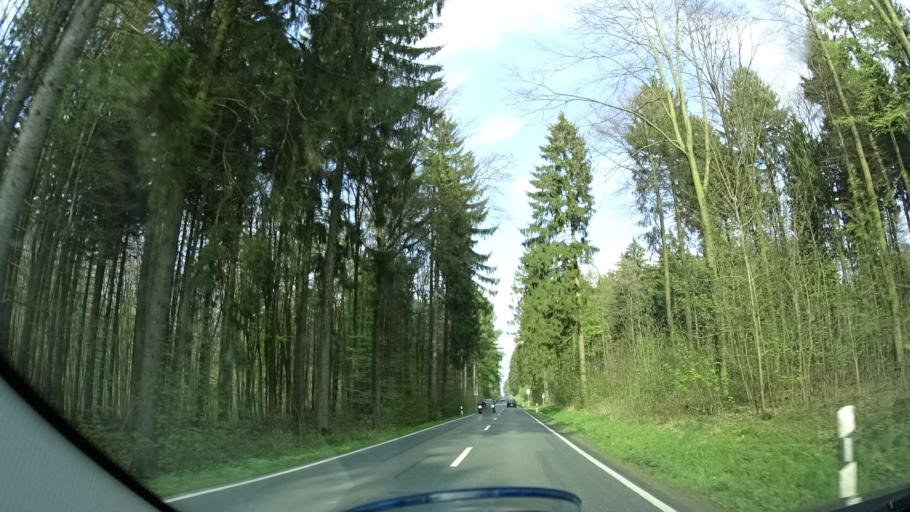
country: DE
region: North Rhine-Westphalia
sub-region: Regierungsbezirk Detmold
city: Wunnenberg
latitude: 51.5552
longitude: 8.6689
